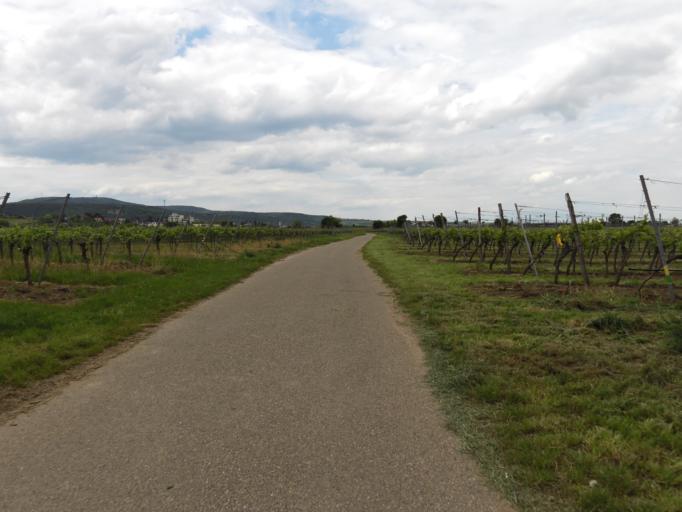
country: DE
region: Rheinland-Pfalz
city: Wachenheim
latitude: 49.4496
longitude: 8.1834
